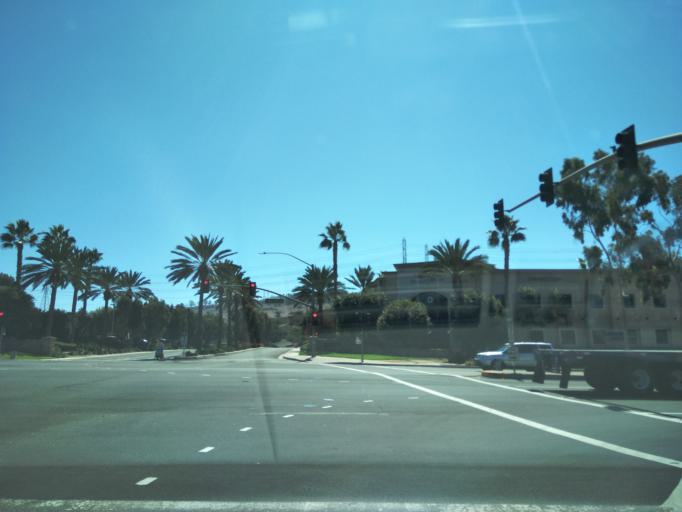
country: US
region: California
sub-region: Orange County
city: San Clemente
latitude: 33.4592
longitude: -117.5924
